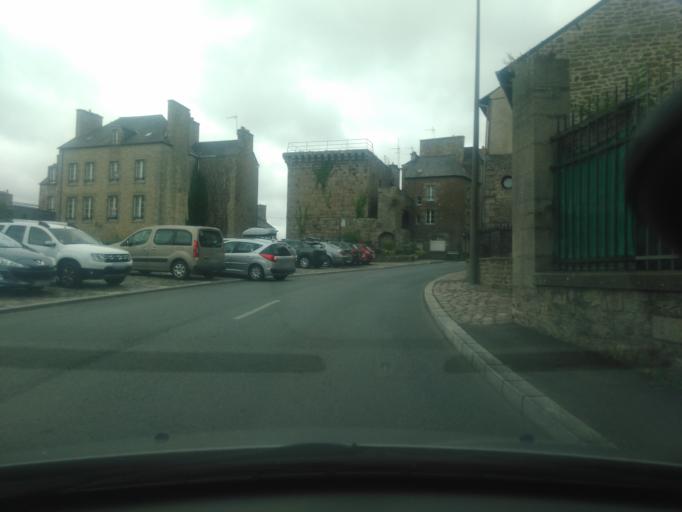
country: FR
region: Brittany
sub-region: Departement des Cotes-d'Armor
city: Lehon
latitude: 48.4501
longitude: -2.0425
